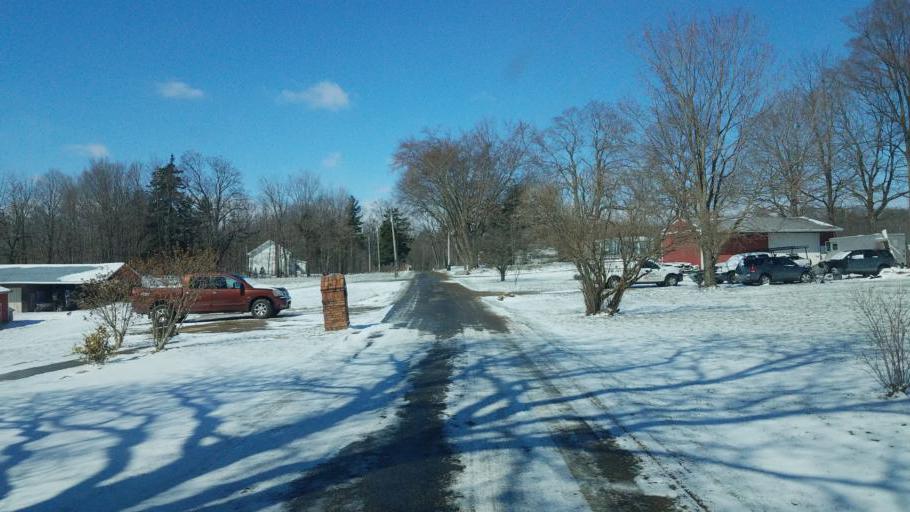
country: US
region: Ohio
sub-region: Knox County
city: Fredericktown
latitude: 40.4838
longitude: -82.6240
